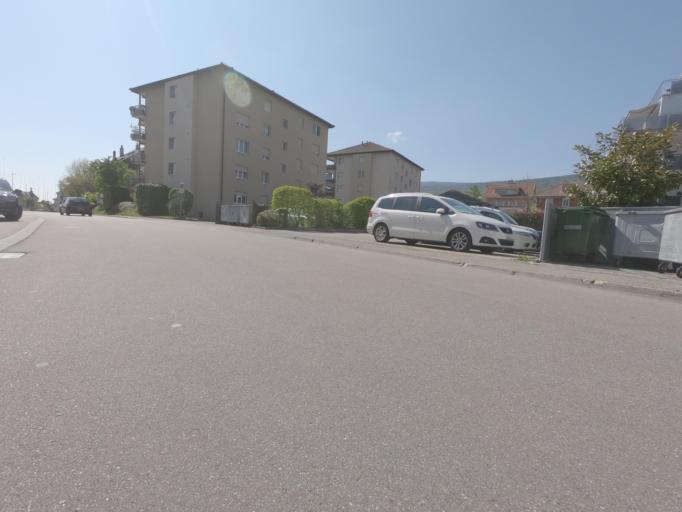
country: CH
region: Neuchatel
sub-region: Neuchatel District
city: Le Landeron
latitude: 47.0548
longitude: 7.0682
